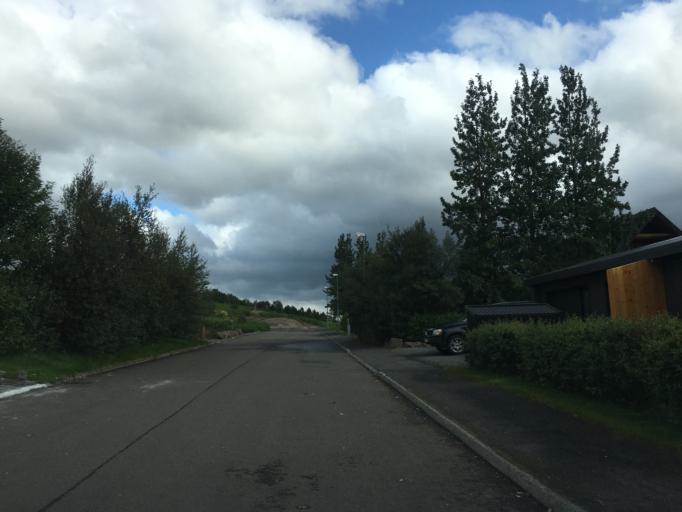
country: IS
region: East
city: Reydarfjoerdur
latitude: 65.0356
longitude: -14.2077
